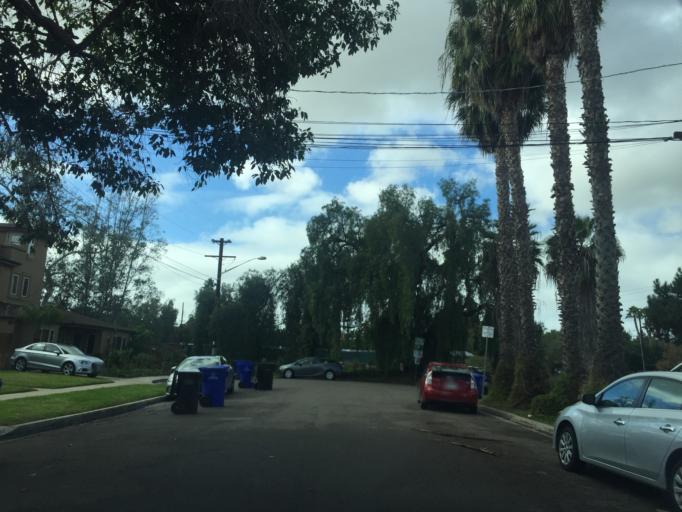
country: US
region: California
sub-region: San Diego County
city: La Jolla
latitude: 32.8044
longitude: -117.2223
